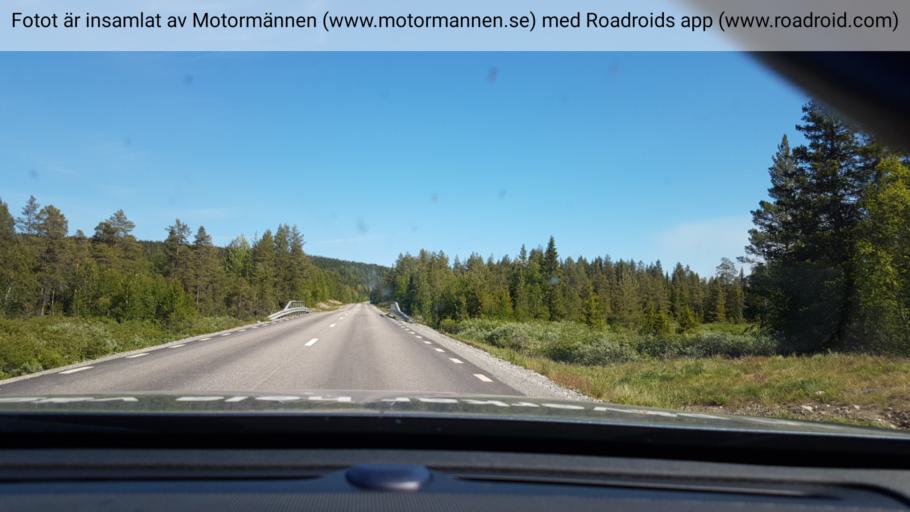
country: SE
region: Vaesterbotten
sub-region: Asele Kommun
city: Insjon
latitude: 64.7214
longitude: 17.6428
